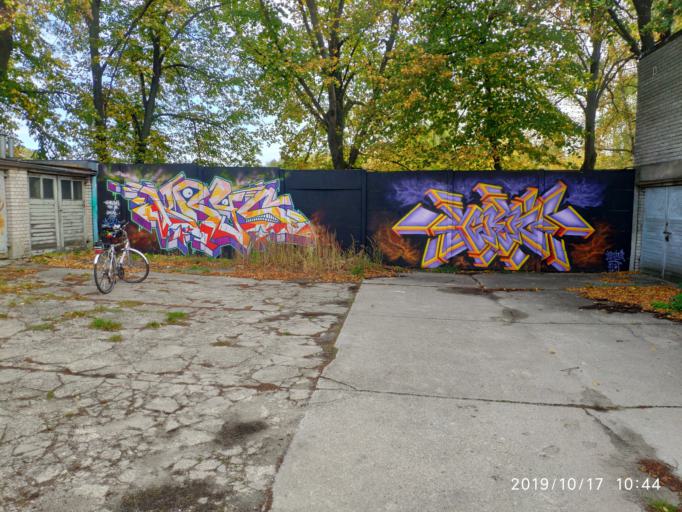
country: PL
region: Lubusz
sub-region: Zielona Gora
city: Zielona Gora
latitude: 51.9442
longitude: 15.5256
